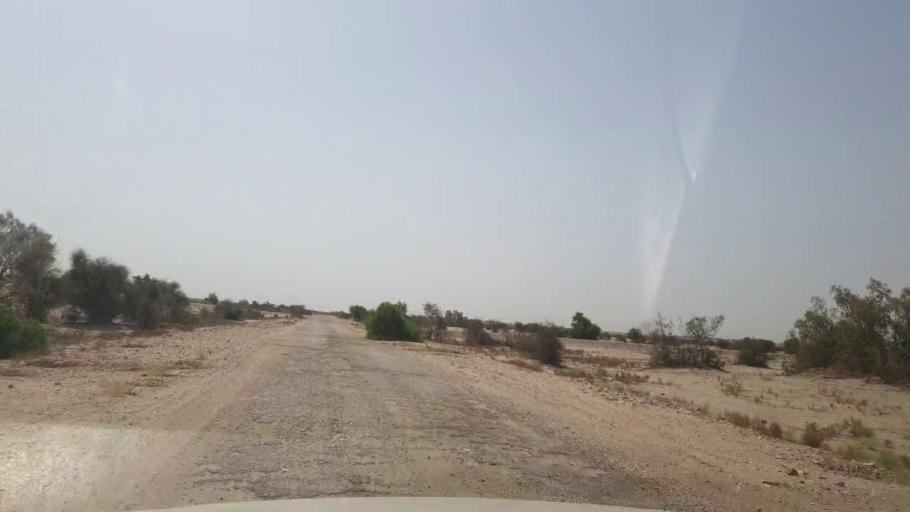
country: PK
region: Sindh
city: Rohri
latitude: 27.4493
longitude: 69.2311
